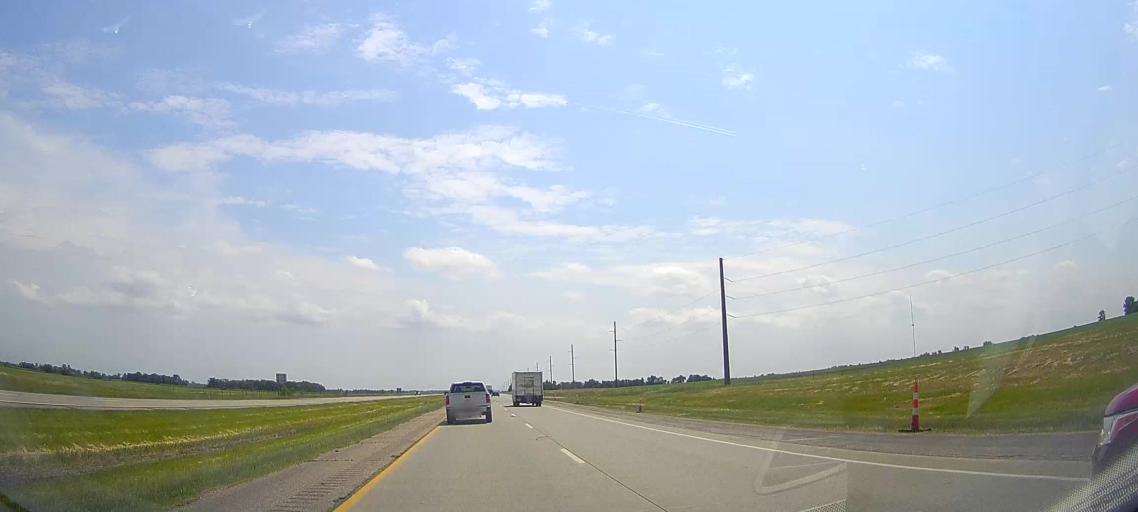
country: US
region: South Dakota
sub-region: Lincoln County
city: Tea
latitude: 43.3852
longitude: -96.7965
